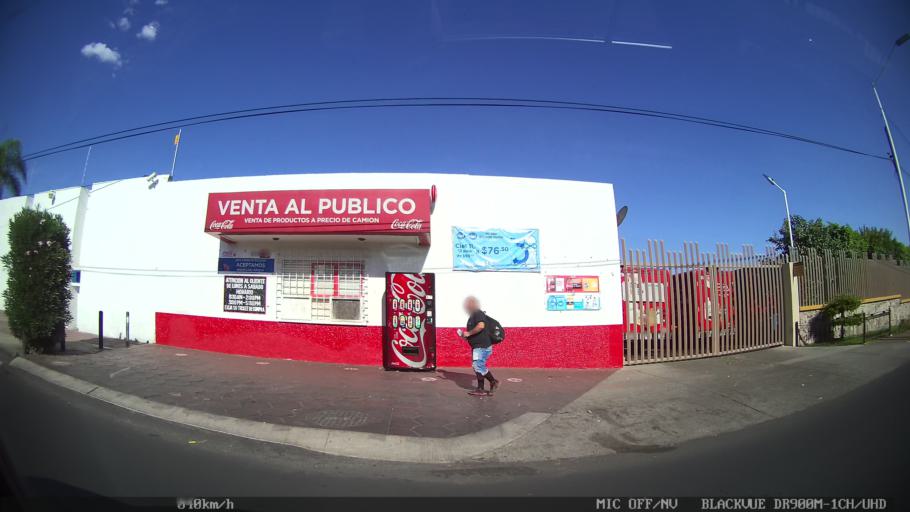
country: MX
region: Jalisco
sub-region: Zapopan
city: Zapopan
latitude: 20.7187
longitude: -103.3180
